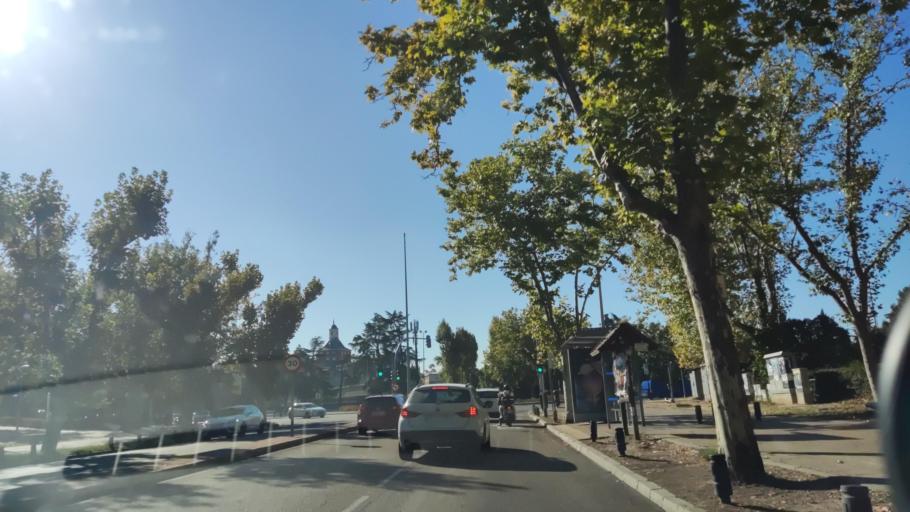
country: ES
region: Madrid
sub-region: Provincia de Madrid
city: Moncloa-Aravaca
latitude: 40.4407
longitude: -3.7267
